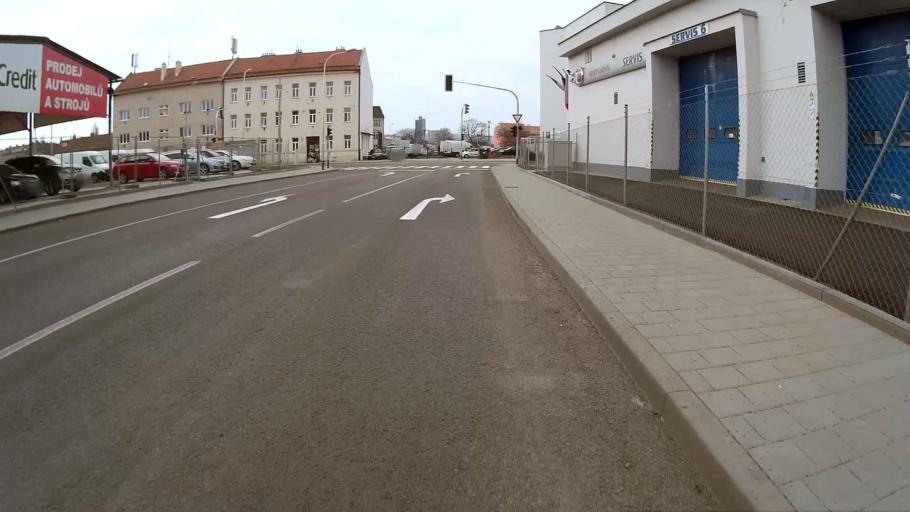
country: CZ
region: South Moravian
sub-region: Mesto Brno
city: Brno
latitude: 49.1816
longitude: 16.6224
